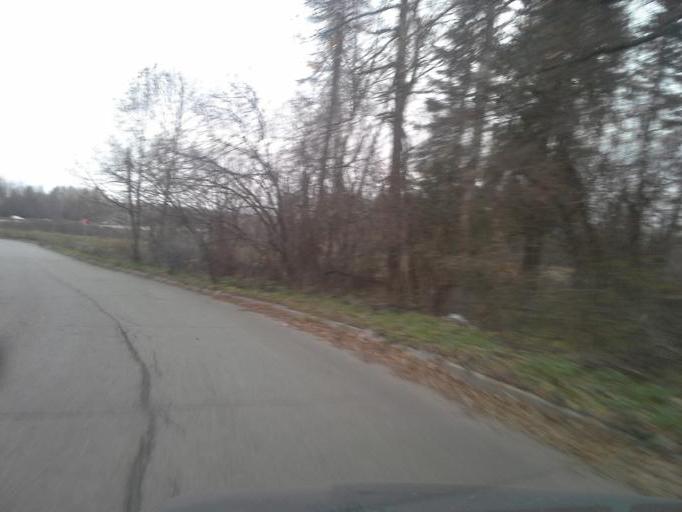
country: RU
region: Moskovskaya
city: Peshki
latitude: 56.1482
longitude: 37.0445
